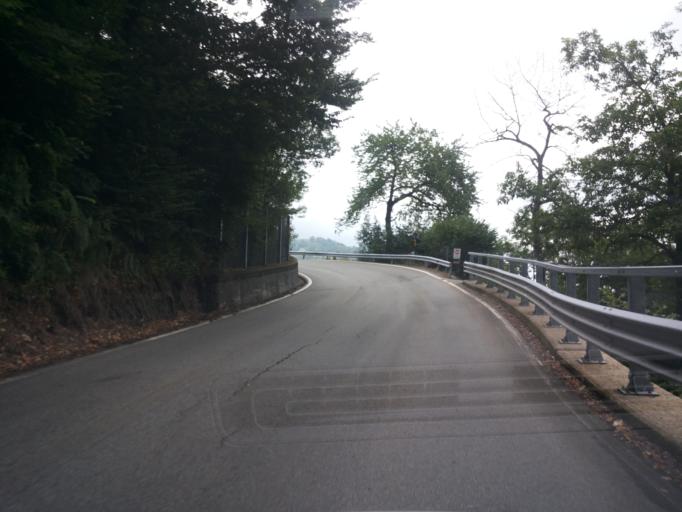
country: IT
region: Piedmont
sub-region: Provincia di Biella
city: Pollone
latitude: 45.6096
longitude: 7.9874
